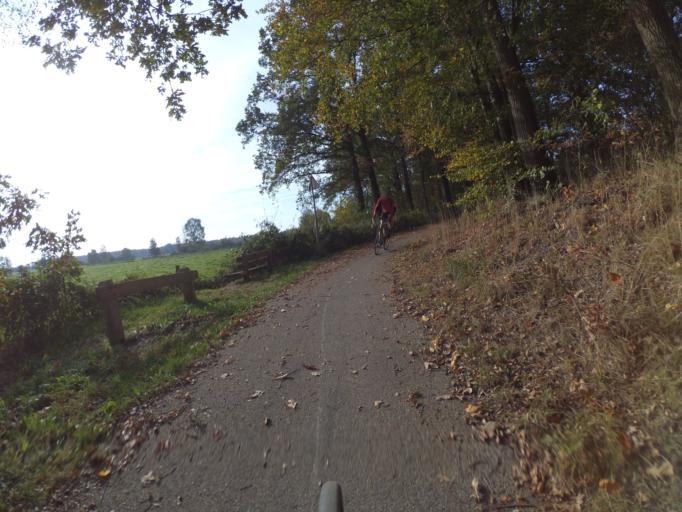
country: NL
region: Overijssel
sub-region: Gemeente Deventer
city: Schalkhaar
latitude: 52.3044
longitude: 6.2539
